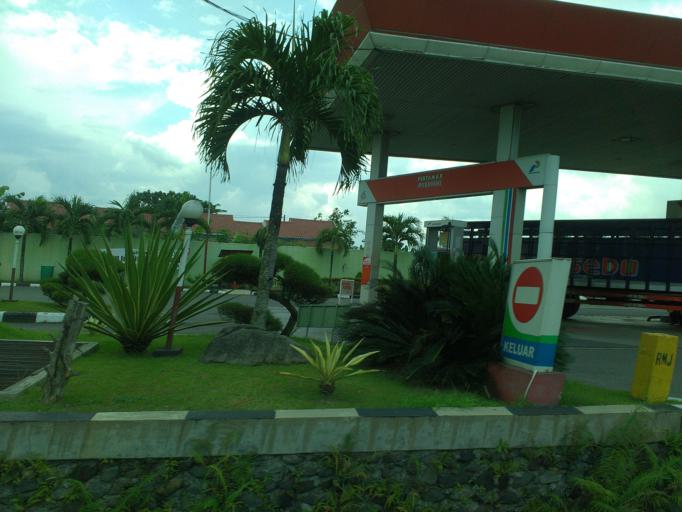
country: ID
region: Central Java
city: Ceper
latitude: -7.6629
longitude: 110.6692
